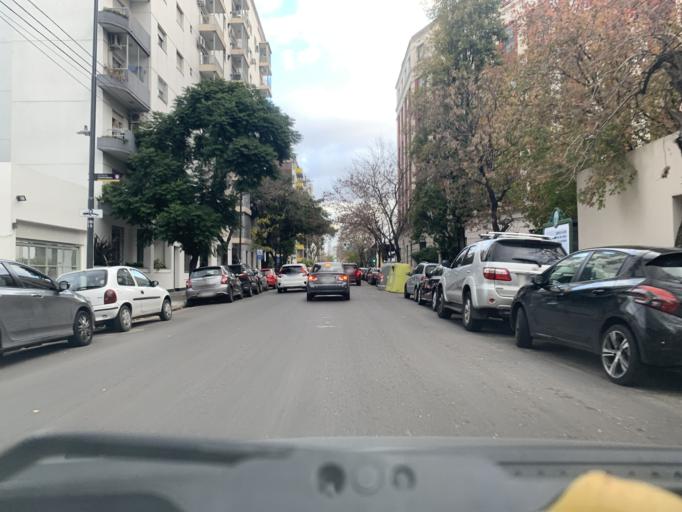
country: AR
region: Buenos Aires F.D.
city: Colegiales
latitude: -34.5794
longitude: -58.4408
